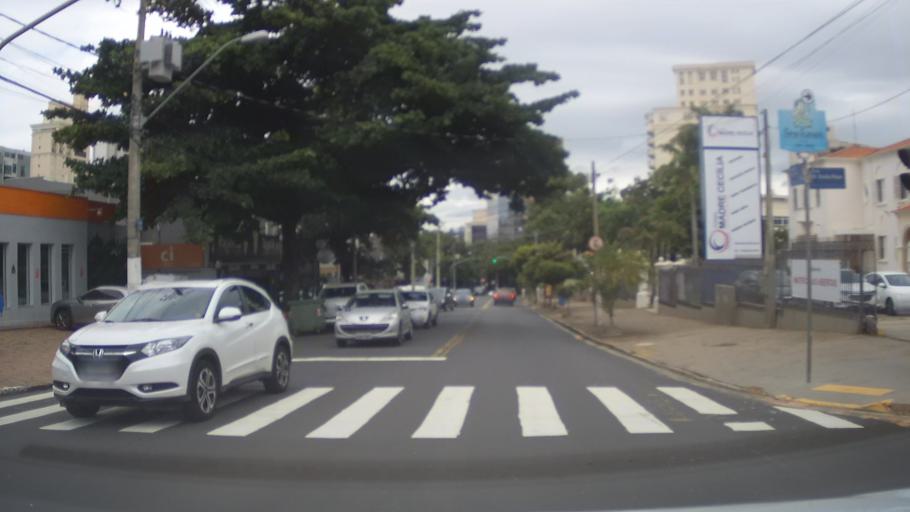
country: BR
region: Sao Paulo
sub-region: Campinas
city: Campinas
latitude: -22.8933
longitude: -47.0510
